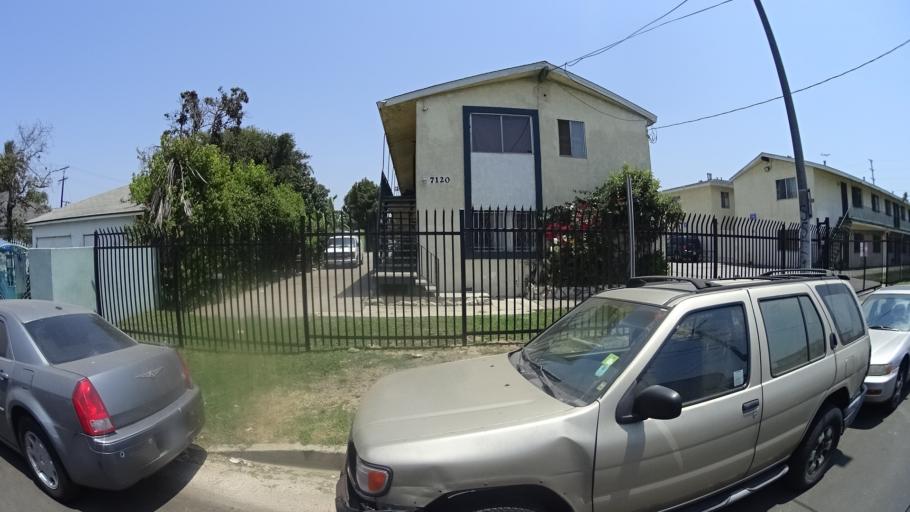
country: US
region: California
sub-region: Los Angeles County
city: Inglewood
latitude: 33.9751
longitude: -118.3338
